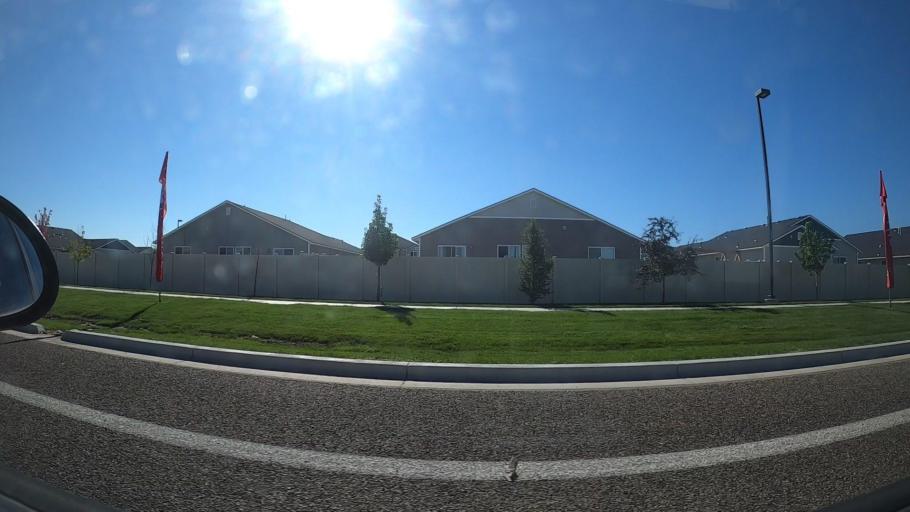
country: US
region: Idaho
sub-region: Canyon County
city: Nampa
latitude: 43.5670
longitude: -116.6131
